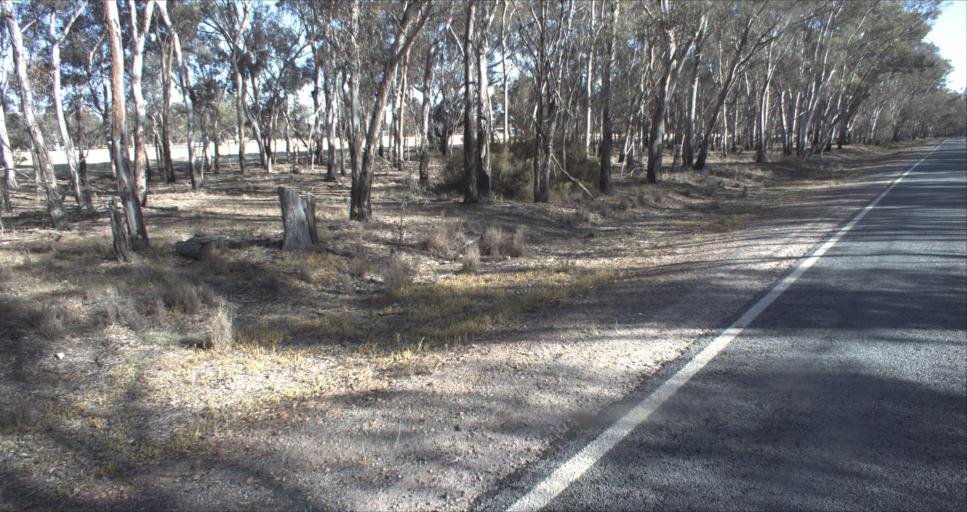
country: AU
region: New South Wales
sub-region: Leeton
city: Leeton
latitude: -34.6280
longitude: 146.3779
